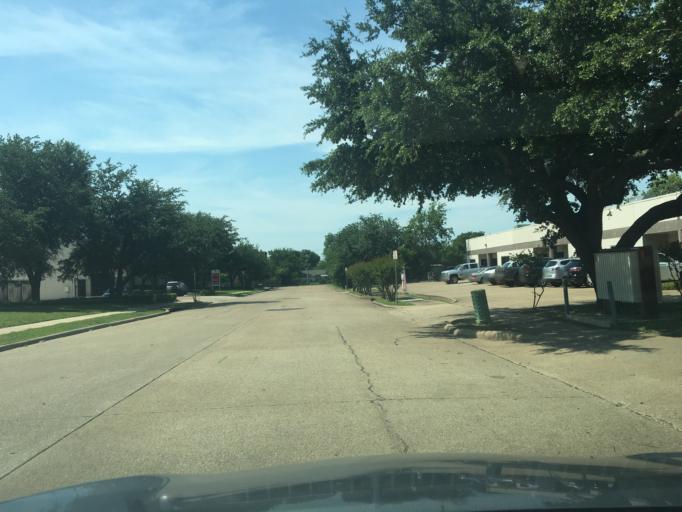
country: US
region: Texas
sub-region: Dallas County
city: Richardson
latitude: 32.9550
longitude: -96.7121
